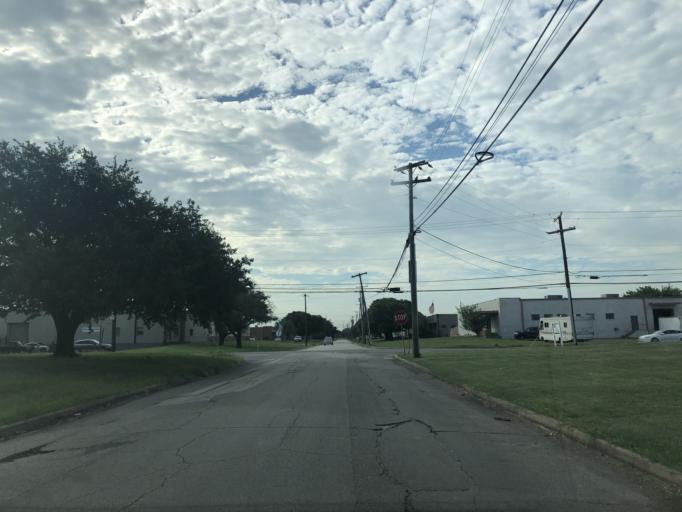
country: US
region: Texas
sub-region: Dallas County
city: Irving
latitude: 32.8173
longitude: -96.8890
